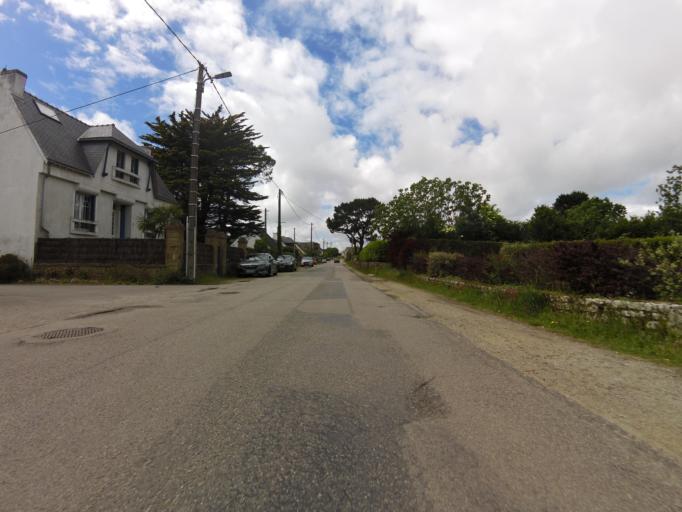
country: FR
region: Brittany
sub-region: Departement du Morbihan
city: Locmariaquer
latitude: 47.5649
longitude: -2.9397
